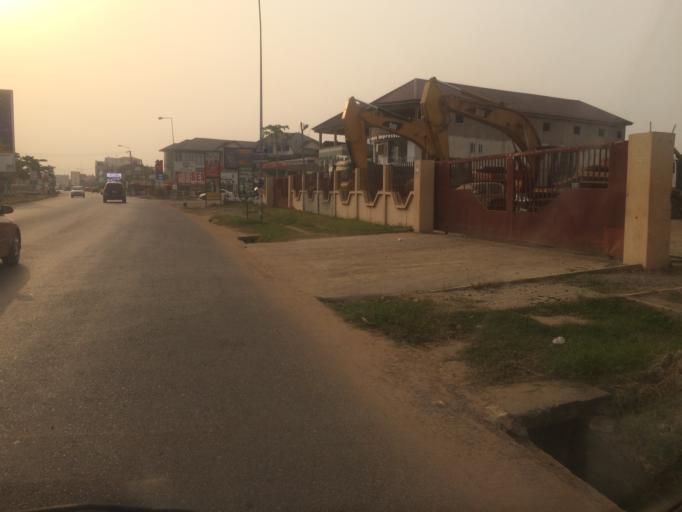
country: GH
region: Greater Accra
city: Nungua
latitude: 5.6368
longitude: -0.1038
